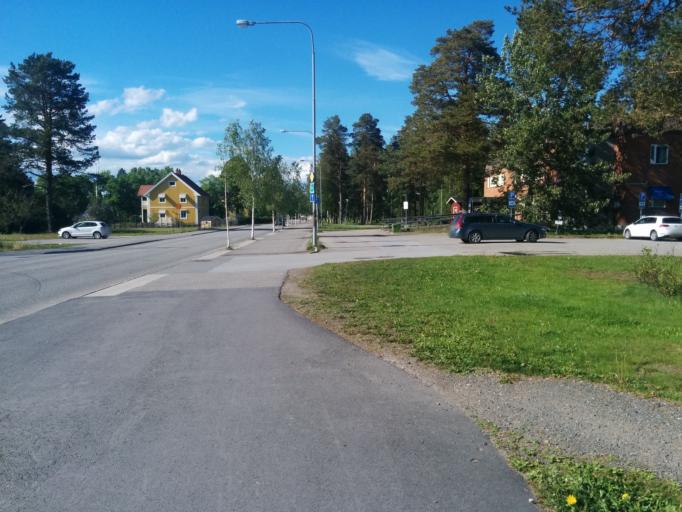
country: SE
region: Vaesterbotten
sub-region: Umea Kommun
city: Hoernefors
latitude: 63.6238
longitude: 19.9086
